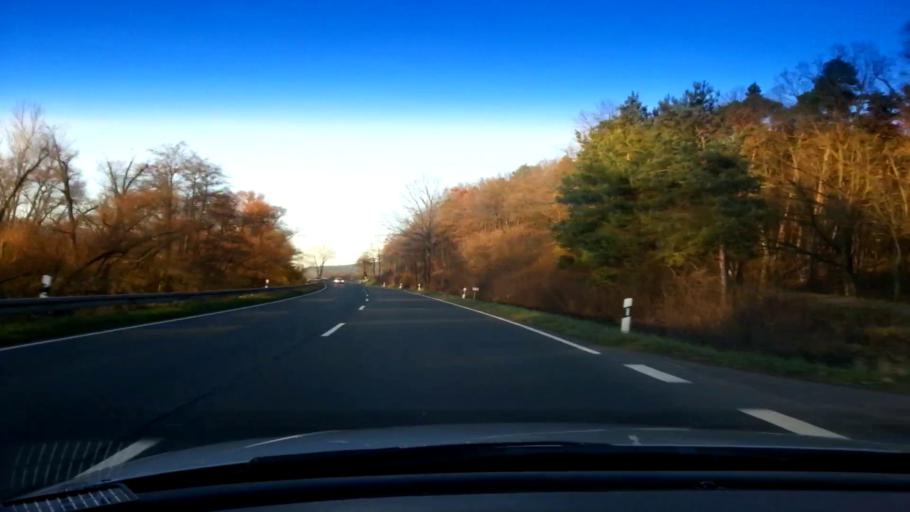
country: DE
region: Bavaria
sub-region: Upper Franconia
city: Rattelsdorf
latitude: 50.0338
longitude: 10.8829
